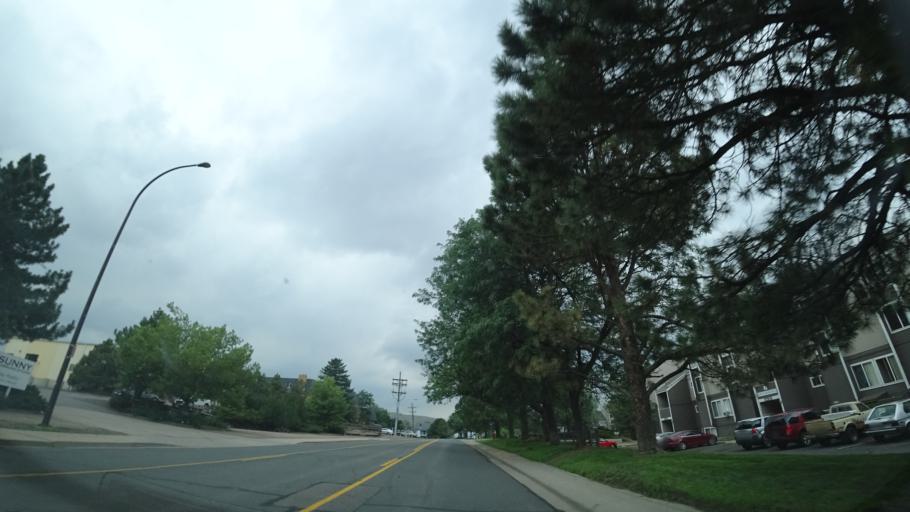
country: US
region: Colorado
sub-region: Jefferson County
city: West Pleasant View
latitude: 39.7123
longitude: -105.1435
